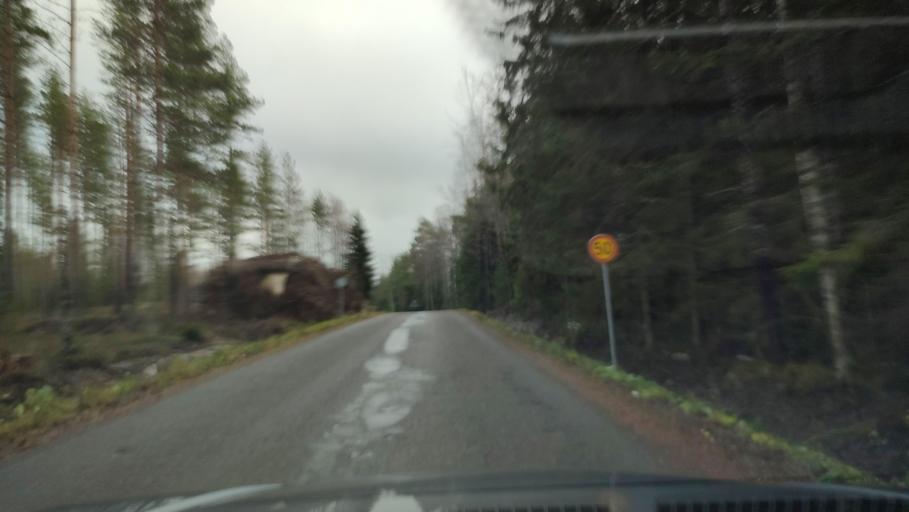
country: FI
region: Southern Ostrobothnia
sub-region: Suupohja
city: Karijoki
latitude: 62.1473
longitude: 21.5578
